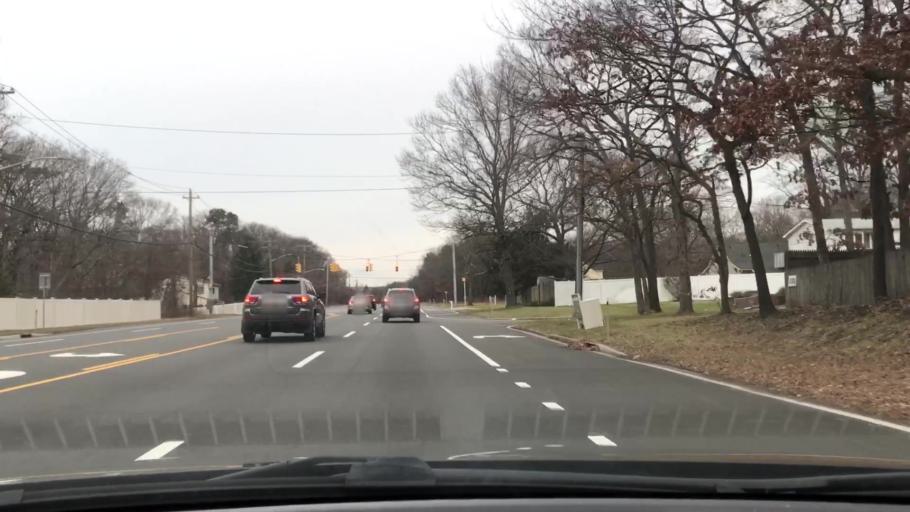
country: US
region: New York
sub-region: Suffolk County
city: North Patchogue
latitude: 40.8008
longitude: -73.0178
